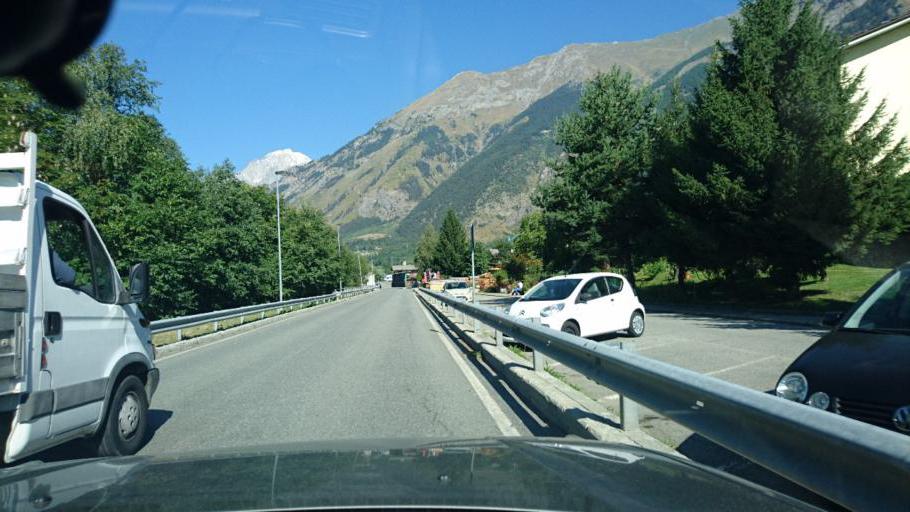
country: IT
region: Aosta Valley
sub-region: Valle d'Aosta
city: Morgex
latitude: 45.7548
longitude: 7.0375
